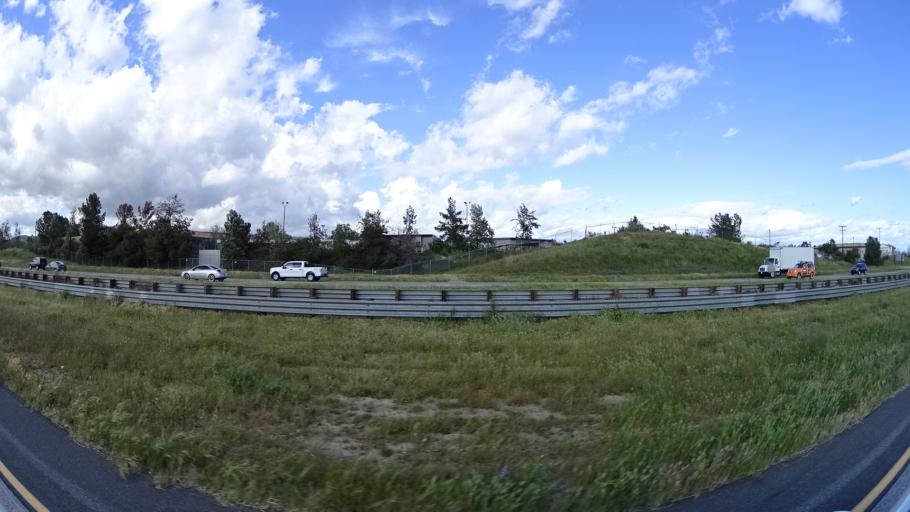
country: US
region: California
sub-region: Riverside County
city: Murrieta
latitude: 33.5703
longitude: -117.2137
